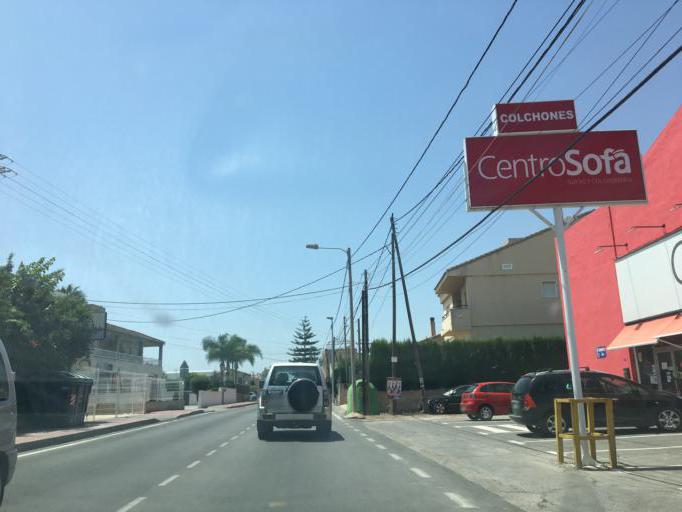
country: ES
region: Murcia
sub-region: Murcia
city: Murcia
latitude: 38.0096
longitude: -1.1110
